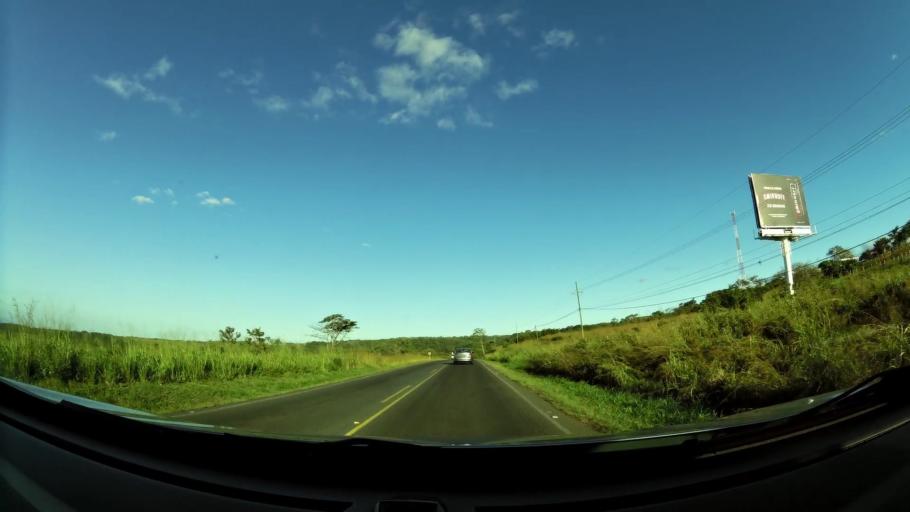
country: CR
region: Puntarenas
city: Miramar
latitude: 10.0969
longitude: -84.8018
